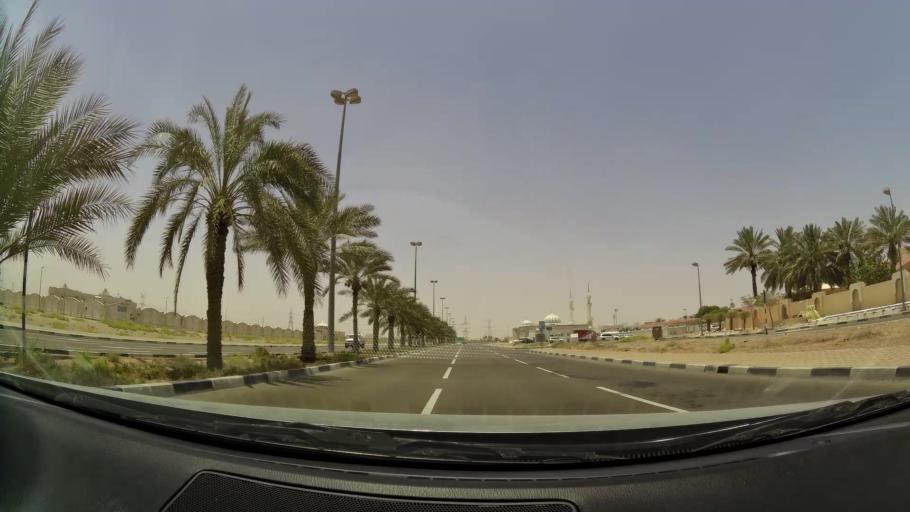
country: OM
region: Al Buraimi
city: Al Buraymi
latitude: 24.2691
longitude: 55.7205
